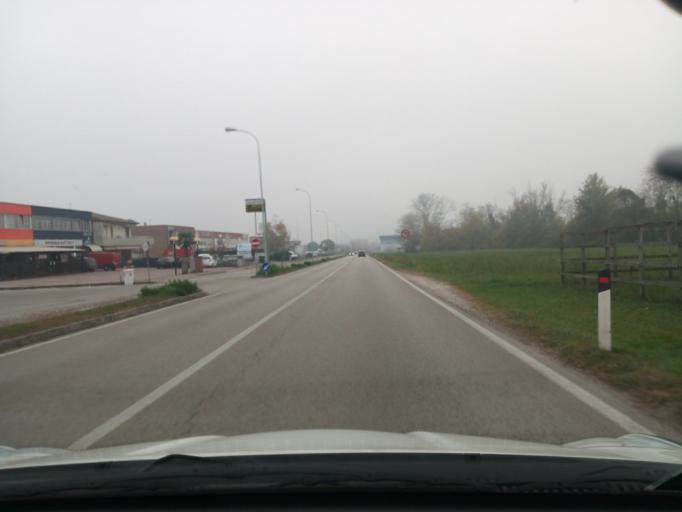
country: IT
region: Veneto
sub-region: Provincia di Vicenza
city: Santorso
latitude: 45.7265
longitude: 11.3877
